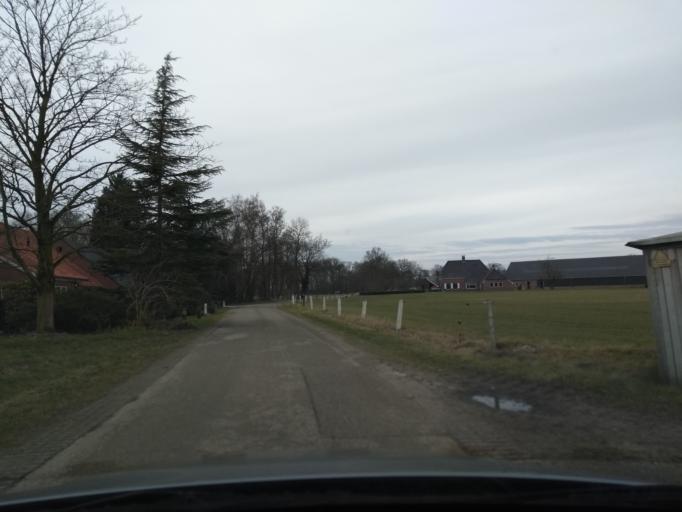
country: NL
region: Overijssel
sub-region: Gemeente Borne
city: Borne
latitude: 52.3307
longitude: 6.7376
